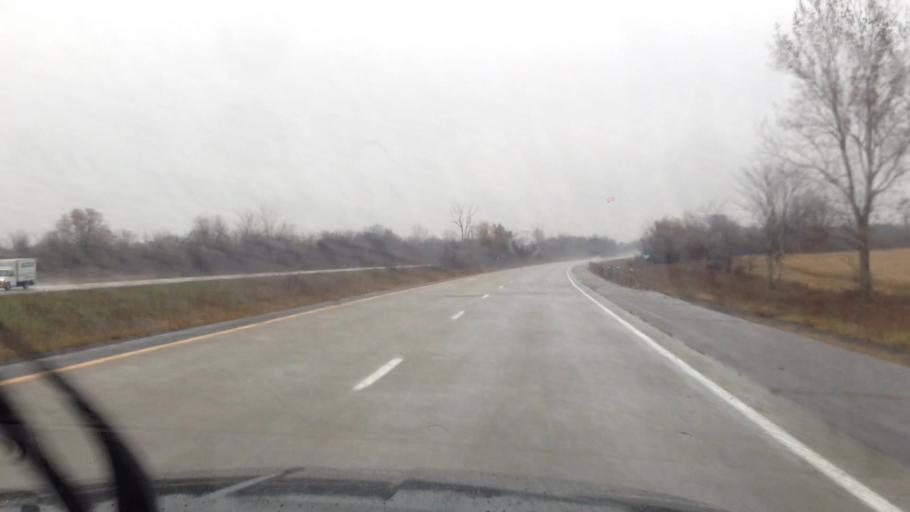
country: CA
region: Ontario
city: Casselman
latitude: 45.3797
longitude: -74.8252
